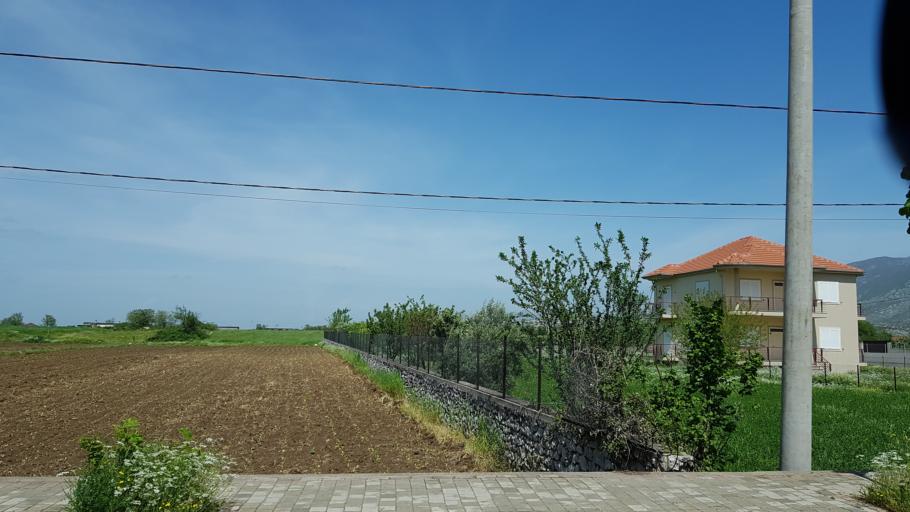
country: AL
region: Shkoder
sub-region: Rrethi i Shkodres
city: Guri i Zi
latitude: 42.1111
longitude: 19.5687
